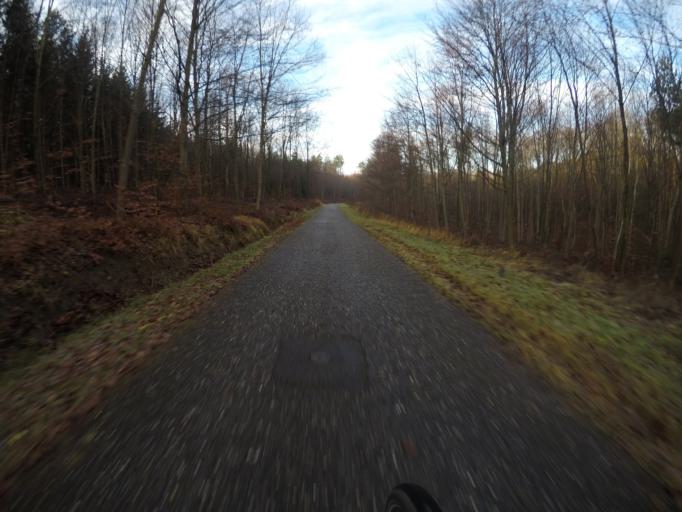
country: DE
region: Baden-Wuerttemberg
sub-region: Regierungsbezirk Stuttgart
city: Sindelfingen
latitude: 48.7240
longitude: 9.0415
